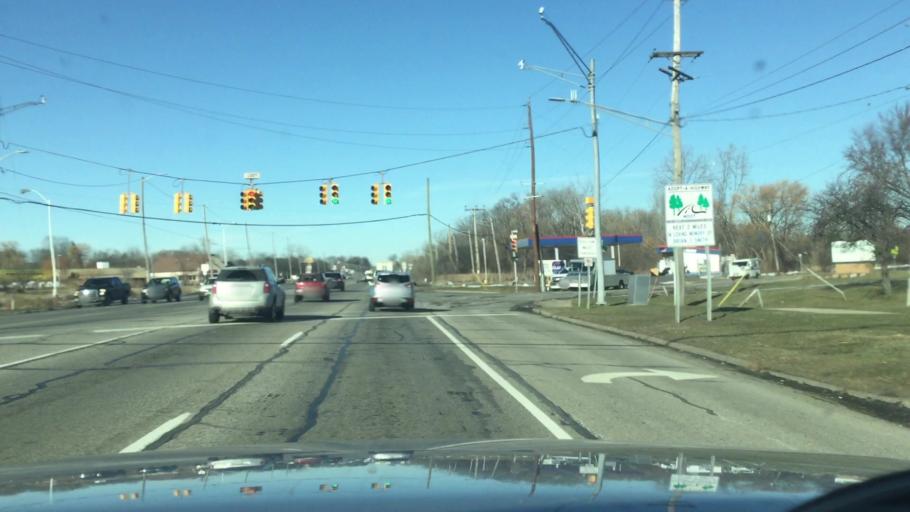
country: US
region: Michigan
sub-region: Oakland County
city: Keego Harbor
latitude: 42.6416
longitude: -83.3551
